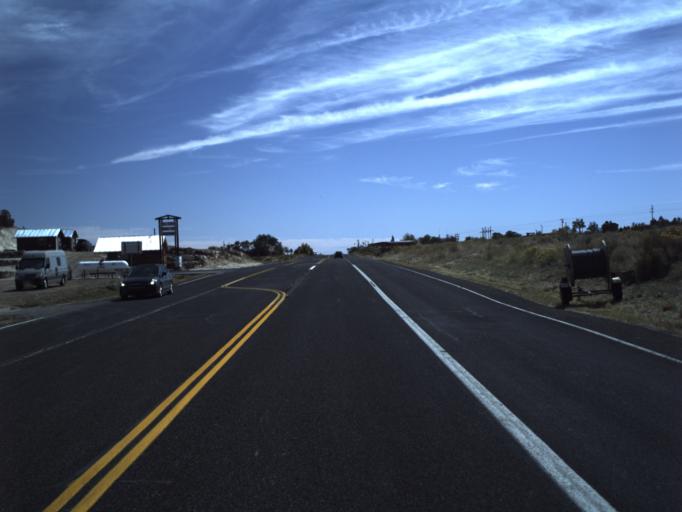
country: US
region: Utah
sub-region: Wayne County
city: Loa
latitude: 37.7734
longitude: -111.6149
